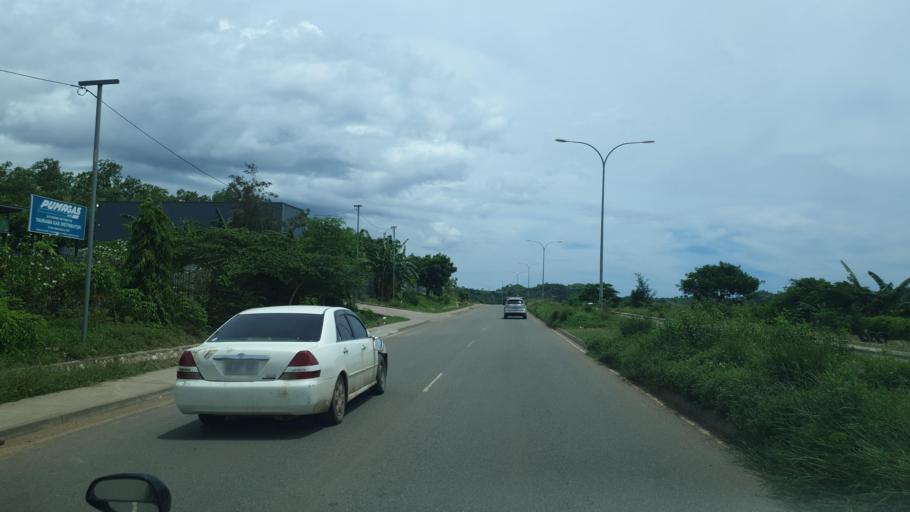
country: PG
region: National Capital
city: Port Moresby
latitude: -9.4977
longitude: 147.2303
